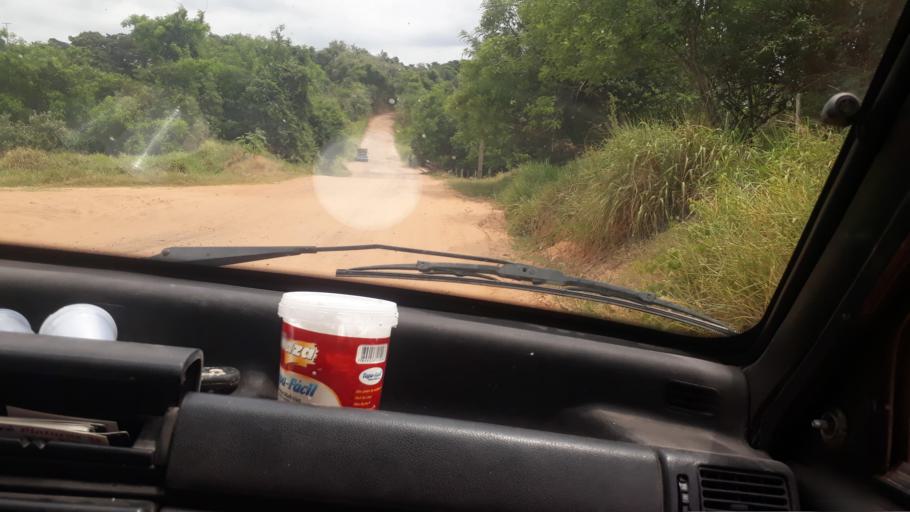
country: BR
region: Sao Paulo
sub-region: Regente Feijo
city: Regente Feijo
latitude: -22.2432
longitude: -51.2984
